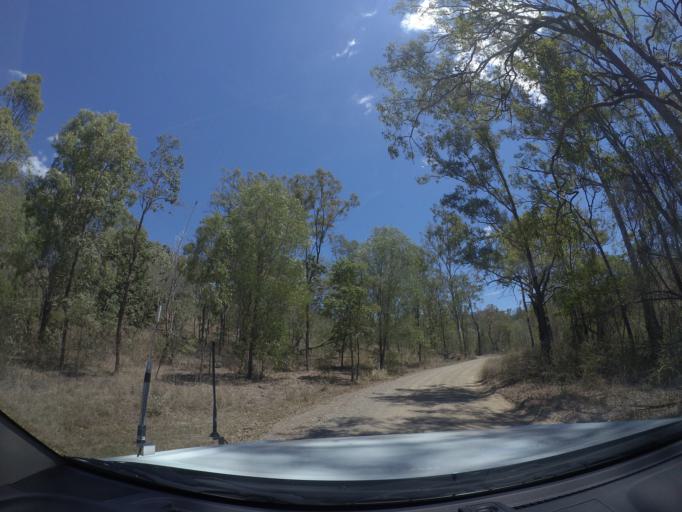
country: AU
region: Queensland
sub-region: Ipswich
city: Springfield Lakes
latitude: -27.8086
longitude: 152.8462
